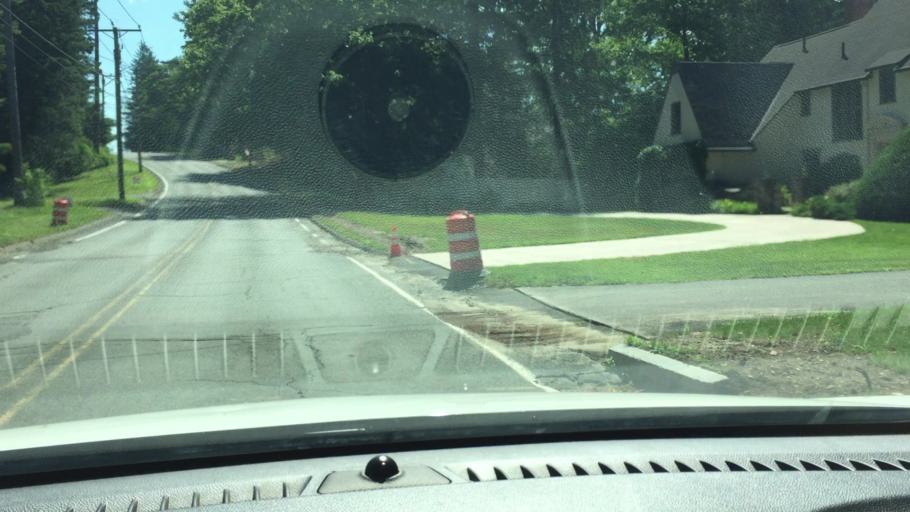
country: US
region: Massachusetts
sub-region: Berkshire County
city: Pittsfield
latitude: 42.4381
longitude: -73.2552
